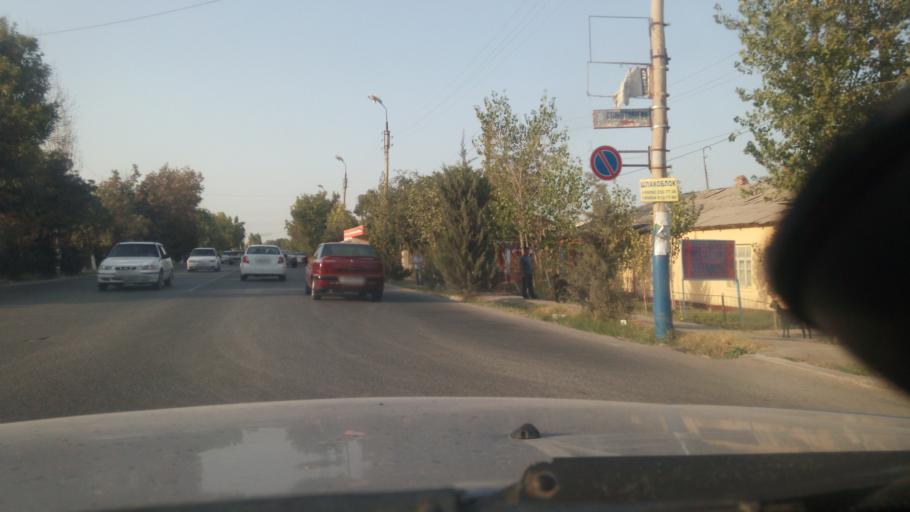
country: UZ
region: Sirdaryo
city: Guliston
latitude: 40.4838
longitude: 68.7770
